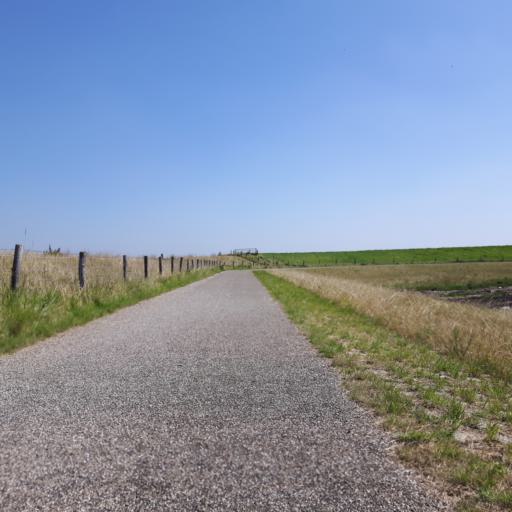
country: NL
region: Zeeland
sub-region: Gemeente Reimerswaal
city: Yerseke
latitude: 51.4301
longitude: 4.0501
